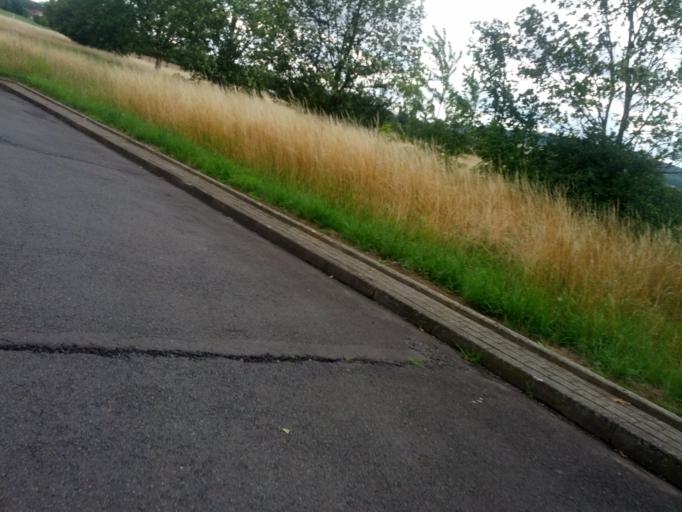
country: DE
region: Thuringia
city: Bischofroda
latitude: 50.9940
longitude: 10.3984
